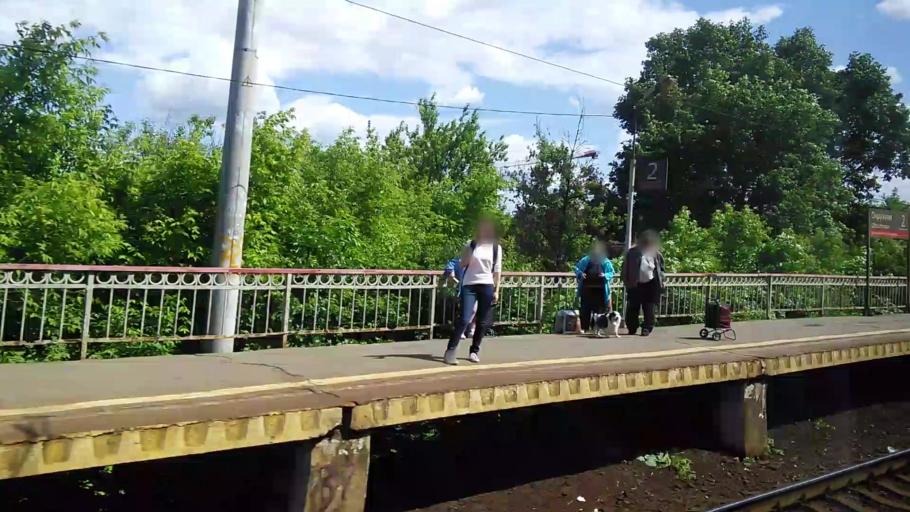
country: RU
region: Moscow
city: Likhobory
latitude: 55.8474
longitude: 37.5742
